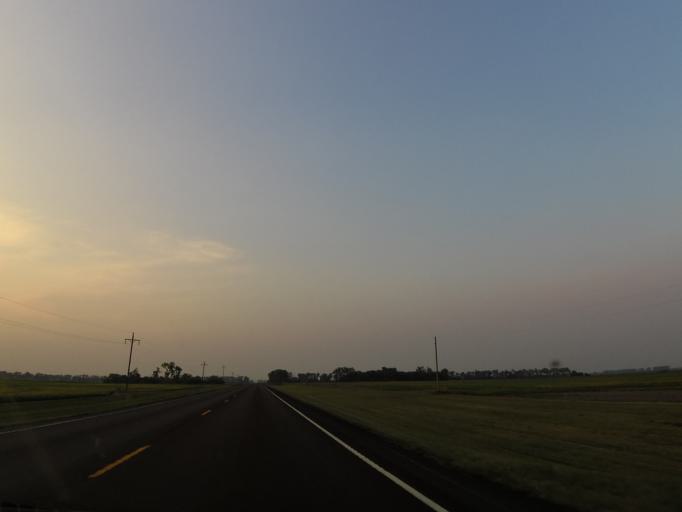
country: US
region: North Dakota
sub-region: Walsh County
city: Park River
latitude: 48.3289
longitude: -97.6223
